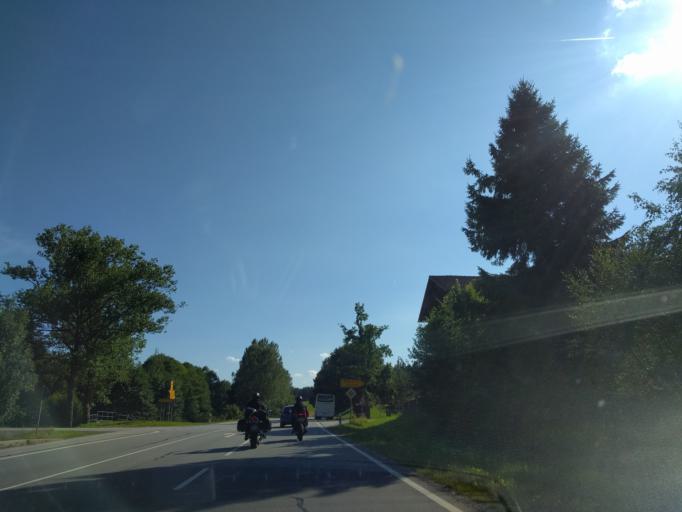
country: DE
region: Bavaria
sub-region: Lower Bavaria
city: Bischofsmais
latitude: 48.9043
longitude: 13.0974
